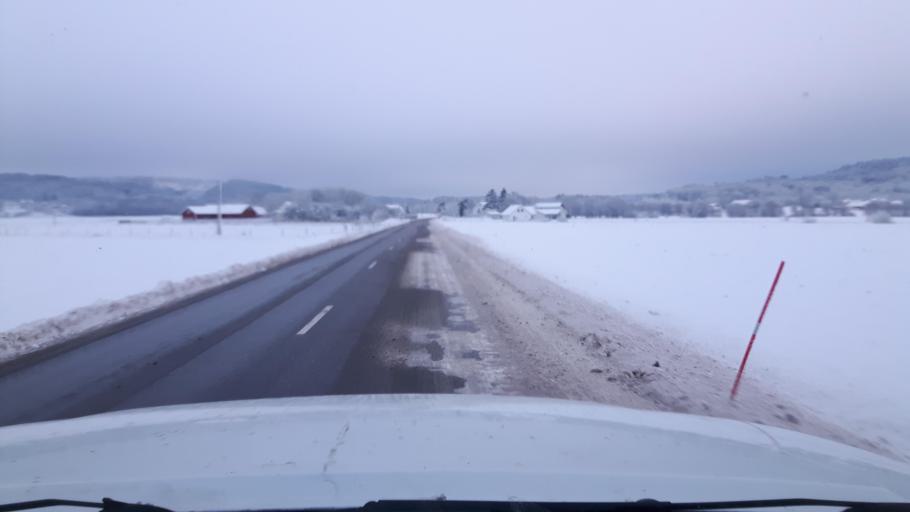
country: SE
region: Halland
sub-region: Kungsbacka Kommun
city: Fjaeras kyrkby
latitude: 57.4271
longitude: 12.1928
